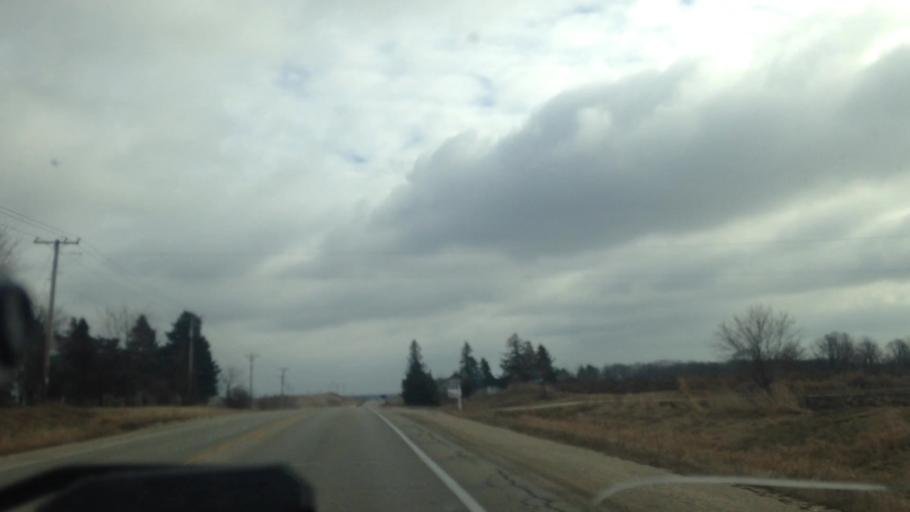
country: US
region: Wisconsin
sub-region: Dodge County
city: Horicon
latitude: 43.4438
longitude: -88.5925
